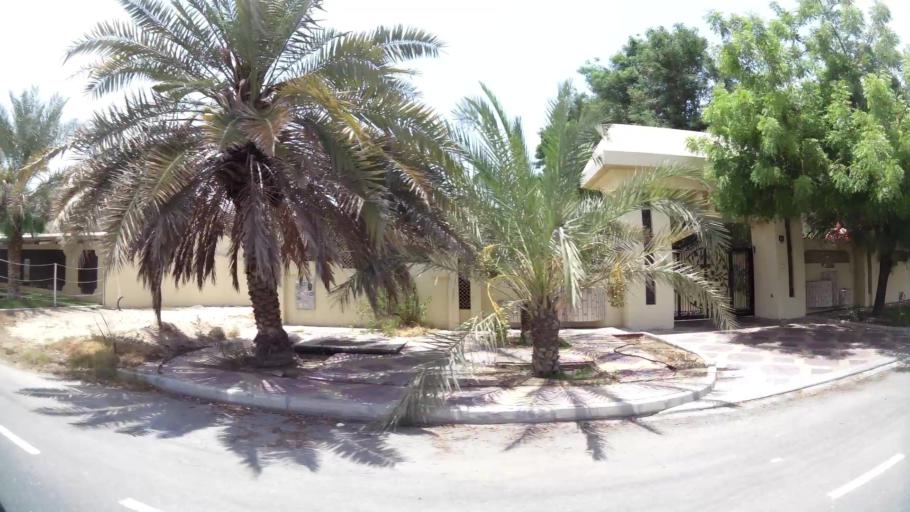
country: AE
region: Ash Shariqah
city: Sharjah
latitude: 25.2054
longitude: 55.3936
